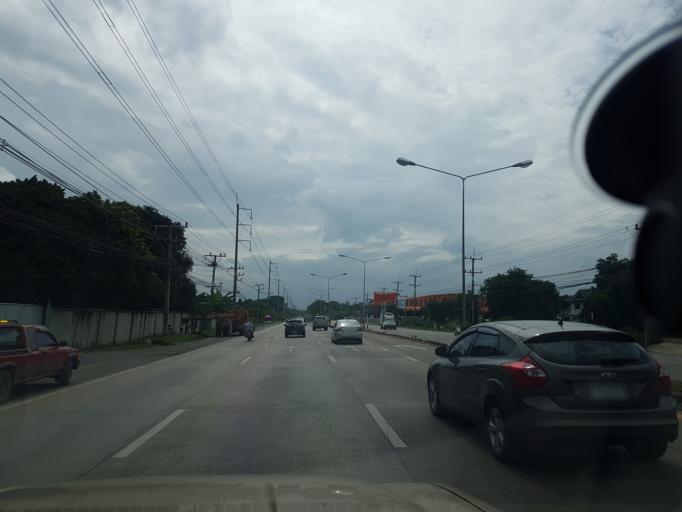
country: TH
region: Sara Buri
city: Phra Phutthabat
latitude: 14.7124
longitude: 100.8261
